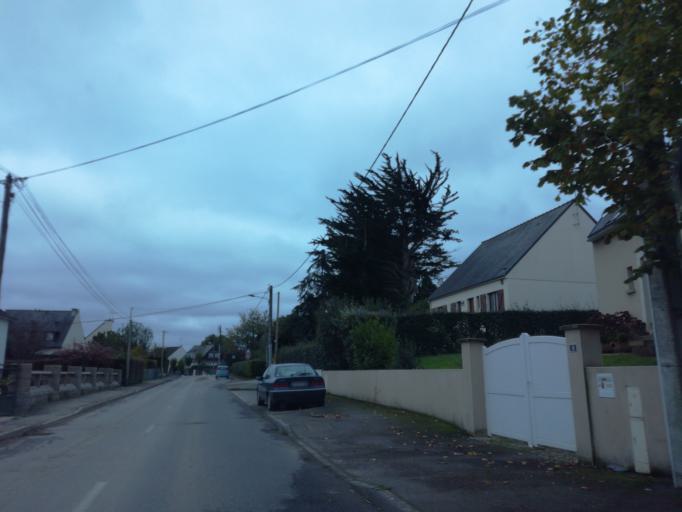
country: FR
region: Brittany
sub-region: Departement d'Ille-et-Vilaine
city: La Richardais
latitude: 48.6087
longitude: -2.0397
